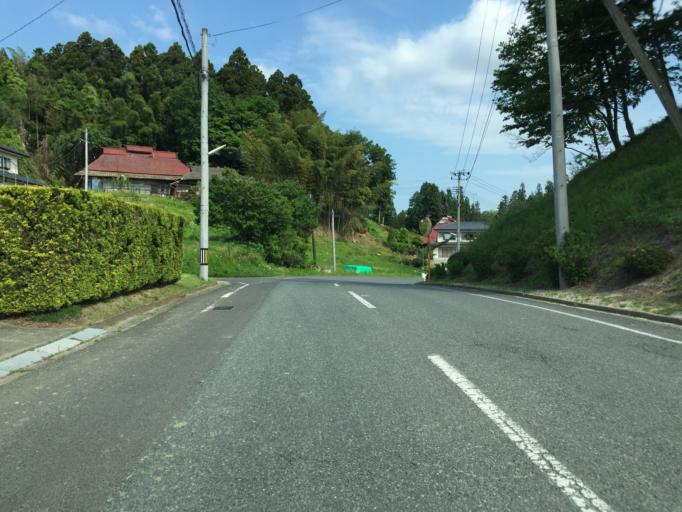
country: JP
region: Fukushima
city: Fukushima-shi
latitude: 37.6633
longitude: 140.4957
